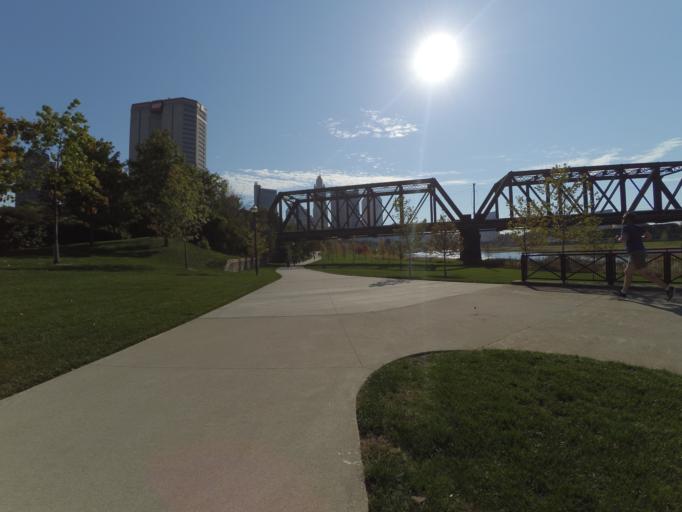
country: US
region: Ohio
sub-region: Franklin County
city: Columbus
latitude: 39.9651
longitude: -83.0087
